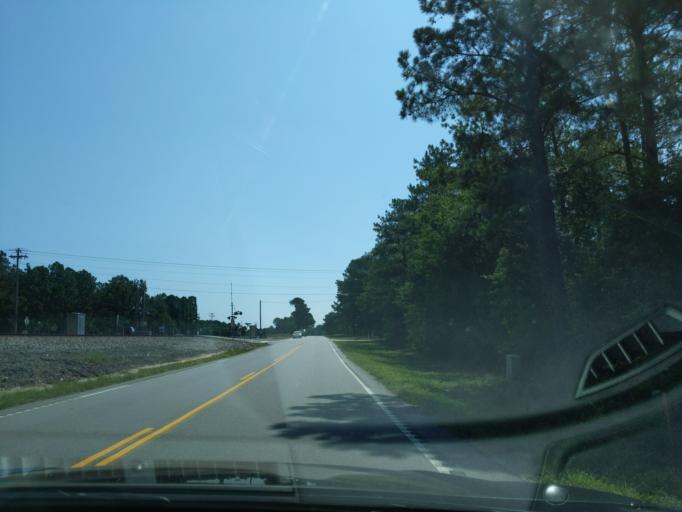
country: US
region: South Carolina
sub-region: Lexington County
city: Red Bank
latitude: 33.9311
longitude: -81.3136
